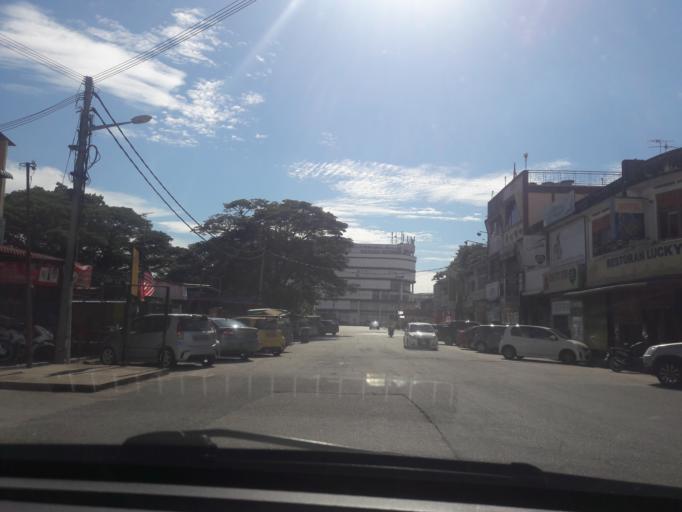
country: MY
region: Kedah
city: Sungai Petani
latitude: 5.6400
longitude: 100.4866
